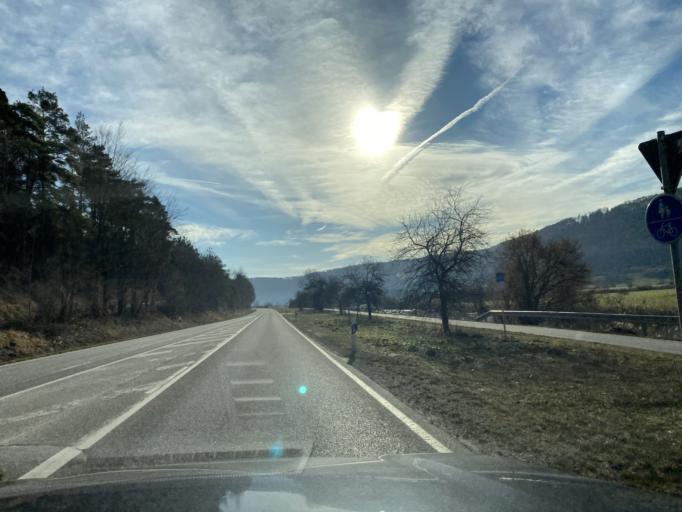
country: DE
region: Bavaria
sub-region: Regierungsbezirk Mittelfranken
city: Greding
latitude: 49.0006
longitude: 11.4043
